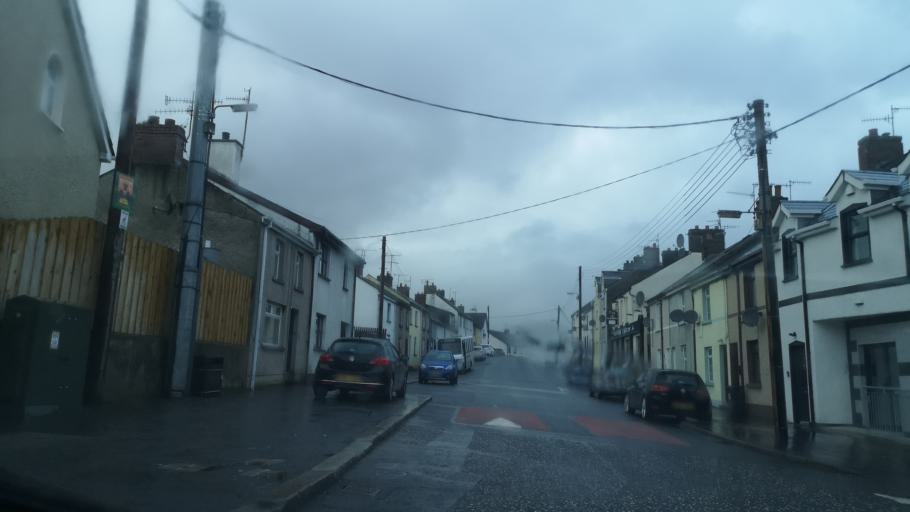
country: GB
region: Northern Ireland
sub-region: Newry and Mourne District
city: Newry
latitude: 54.1766
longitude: -6.3290
